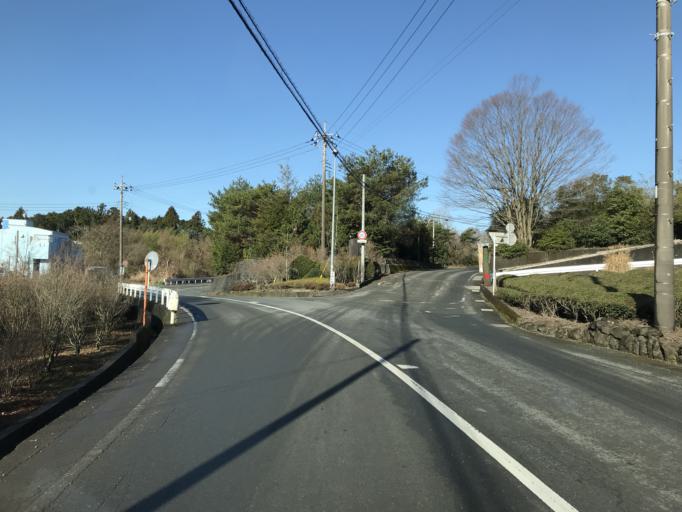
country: JP
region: Shizuoka
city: Fujinomiya
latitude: 35.2393
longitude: 138.6657
